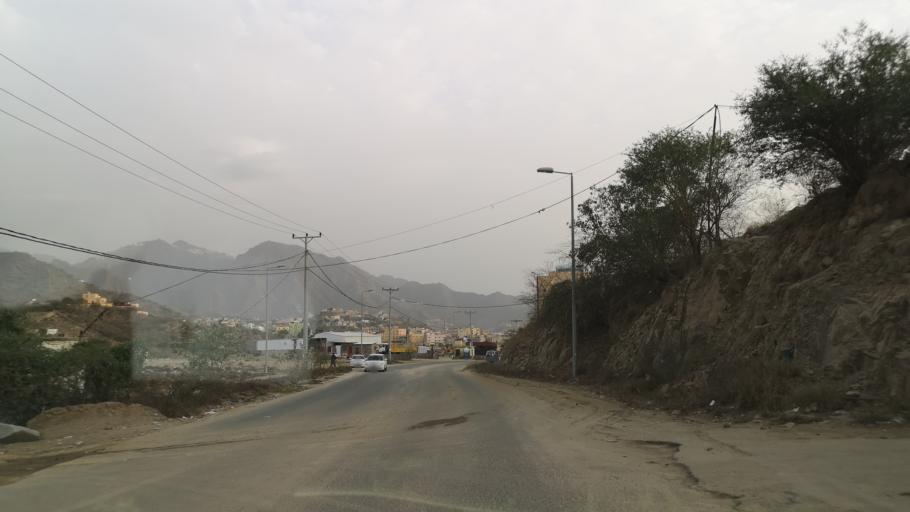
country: YE
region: Sa'dah
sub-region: Monabbih
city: Suq al Khamis
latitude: 17.3620
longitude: 43.1288
